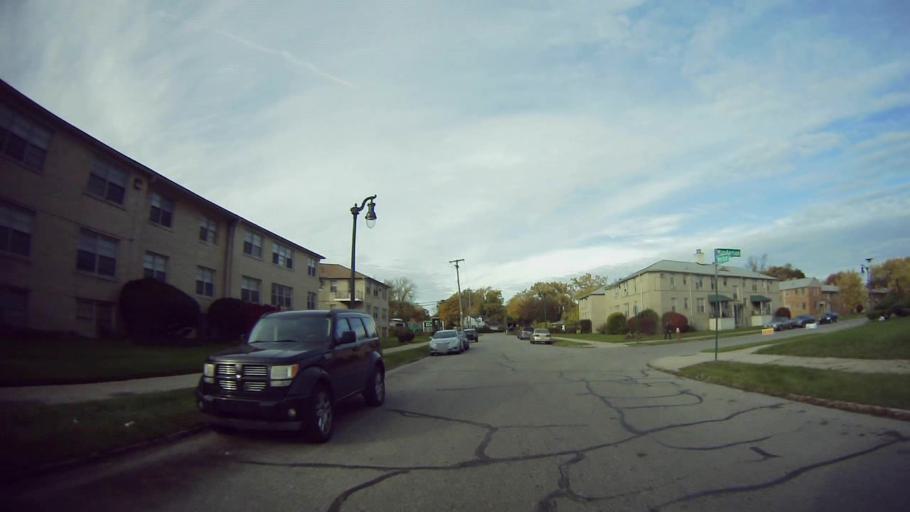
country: US
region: Michigan
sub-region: Wayne County
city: Highland Park
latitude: 42.4181
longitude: -83.1152
